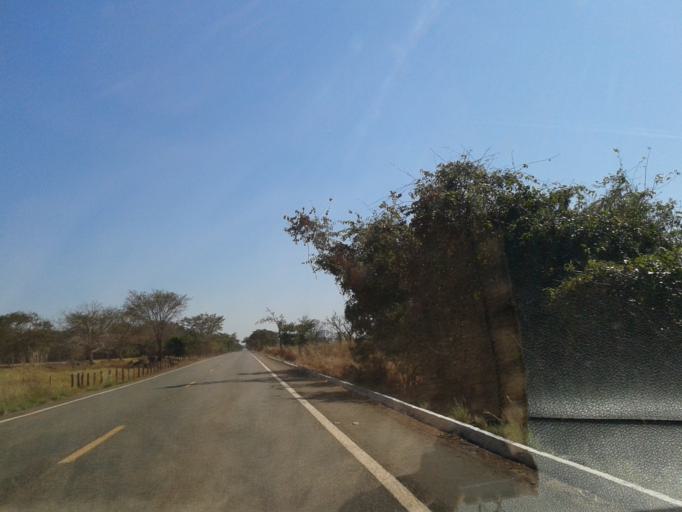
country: BR
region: Goias
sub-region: Sao Miguel Do Araguaia
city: Sao Miguel do Araguaia
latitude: -13.9084
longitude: -50.3251
